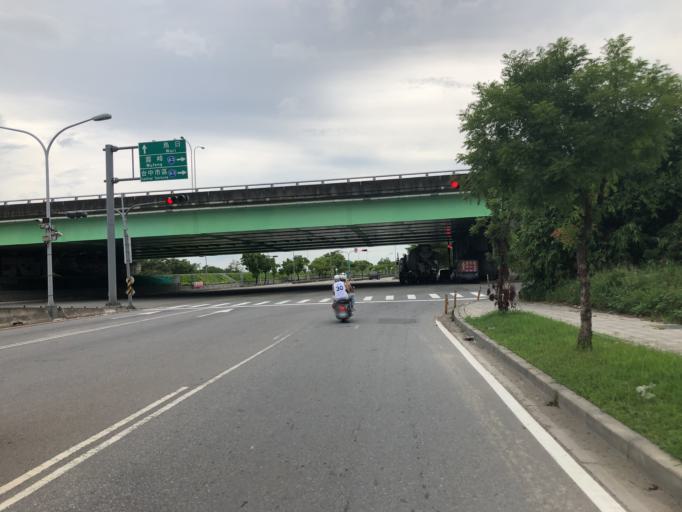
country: TW
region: Taiwan
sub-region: Taichung City
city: Taichung
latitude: 24.0832
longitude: 120.6649
